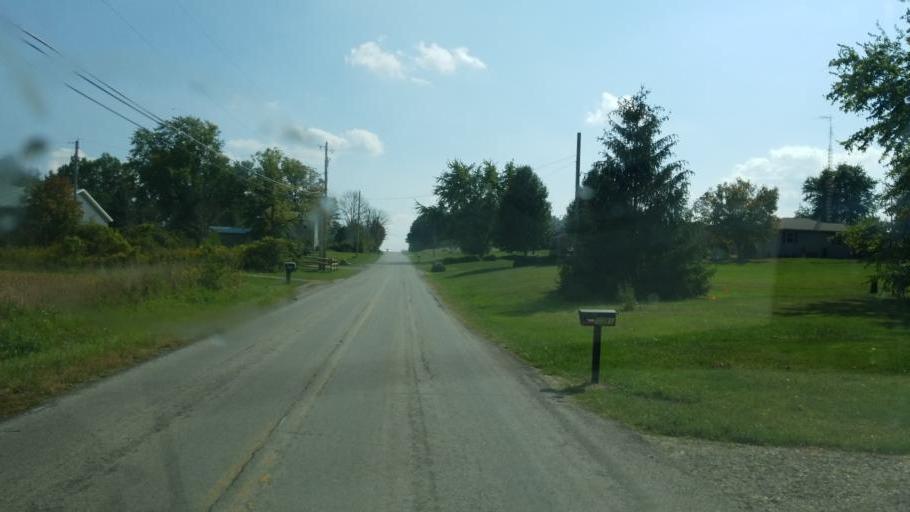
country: US
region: Ohio
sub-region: Richland County
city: Ontario
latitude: 40.7885
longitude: -82.6291
